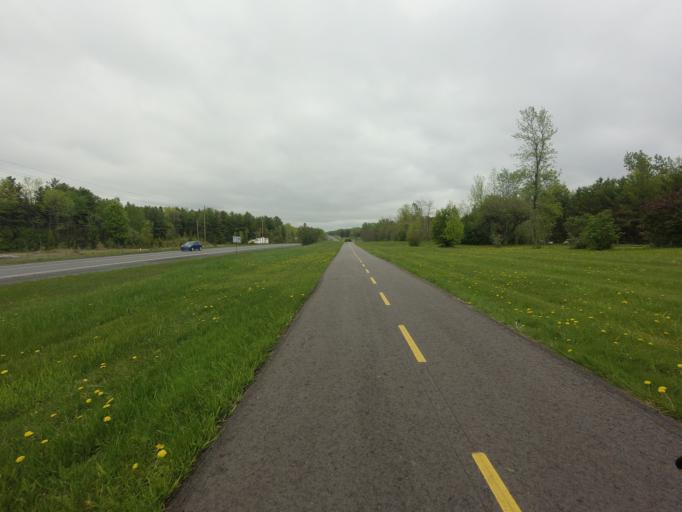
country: CA
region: Ontario
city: Cornwall
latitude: 45.0341
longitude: -74.8333
